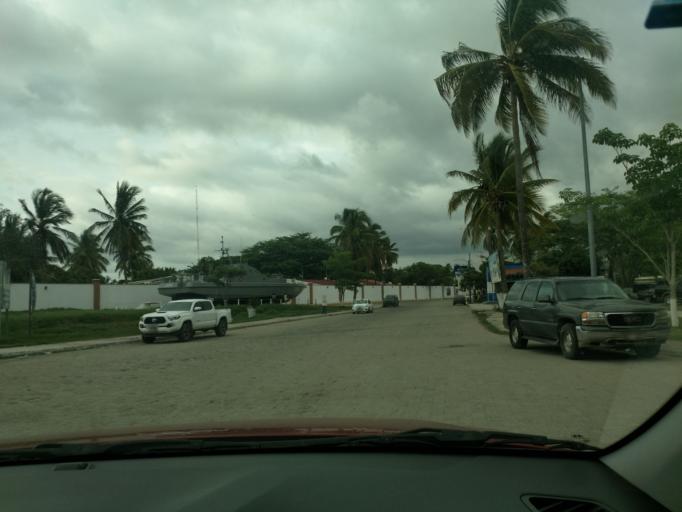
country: MX
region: Nayarit
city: San Blas
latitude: 21.5304
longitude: -105.2852
